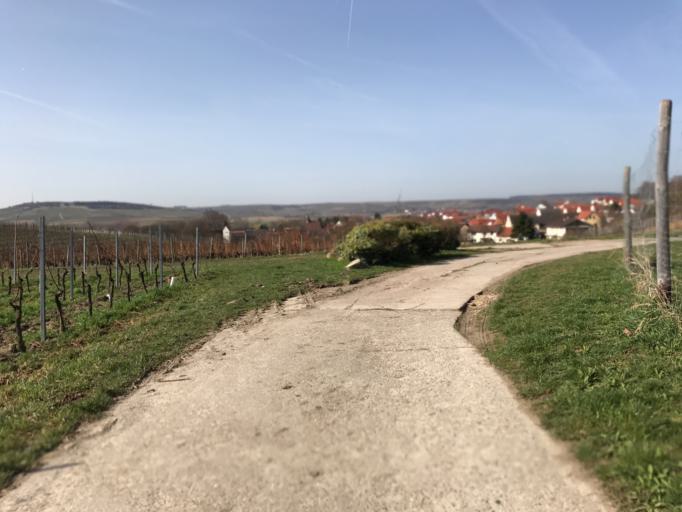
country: DE
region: Rheinland-Pfalz
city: Stadecken-Elsheim
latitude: 49.9167
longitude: 8.1285
